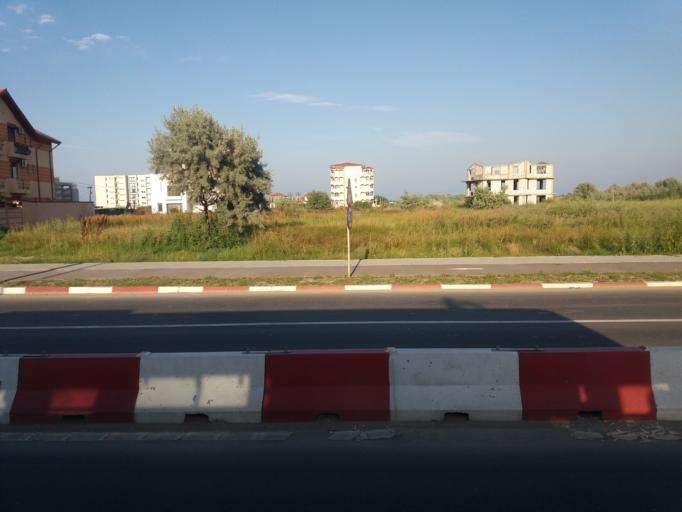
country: RO
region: Constanta
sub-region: Comuna Navodari
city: Navodari
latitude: 44.2913
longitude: 28.6192
